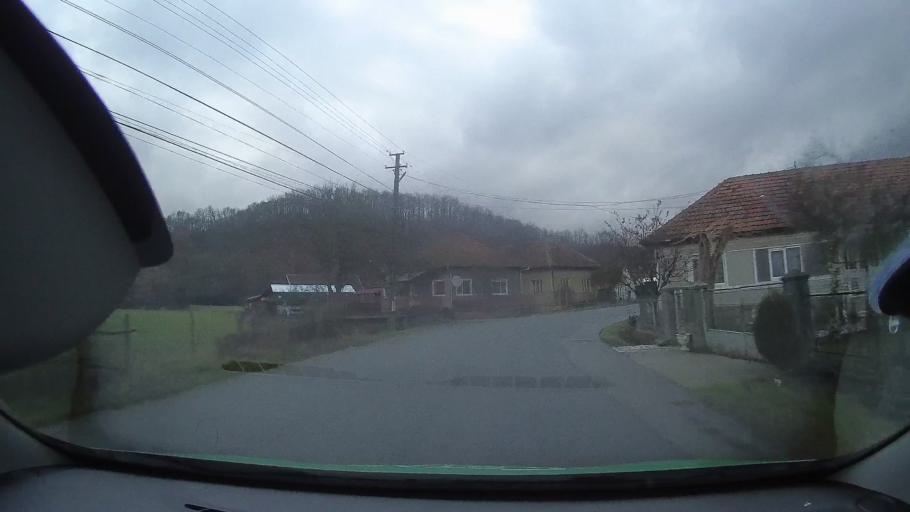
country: RO
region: Hunedoara
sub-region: Comuna Baia de Cris
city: Baia de Cris
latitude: 46.1908
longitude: 22.7147
